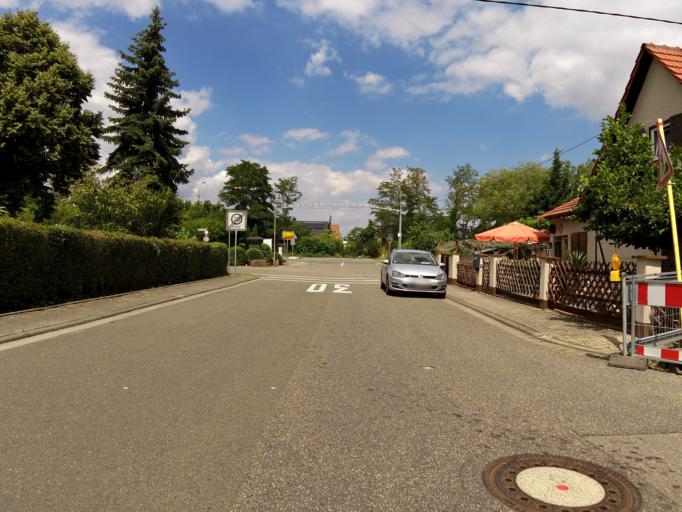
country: DE
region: Rheinland-Pfalz
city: Birkenheide
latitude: 49.4788
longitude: 8.2583
